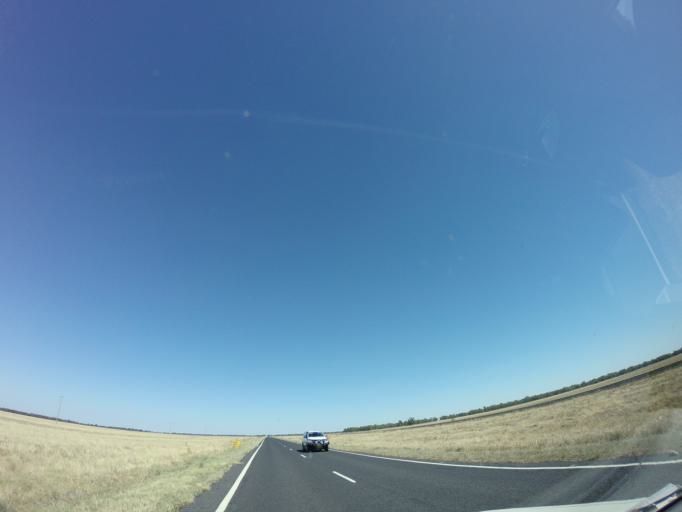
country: AU
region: New South Wales
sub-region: Bogan
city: Nyngan
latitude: -31.7473
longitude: 147.5460
